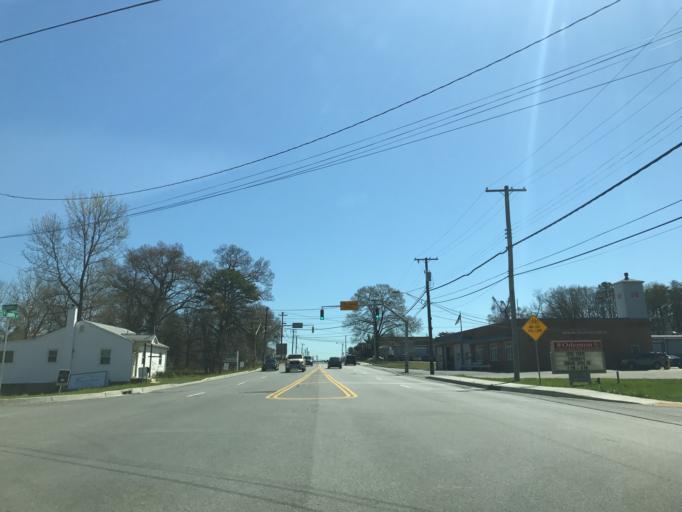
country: US
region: Maryland
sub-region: Anne Arundel County
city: Odenton
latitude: 39.0910
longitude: -76.7120
